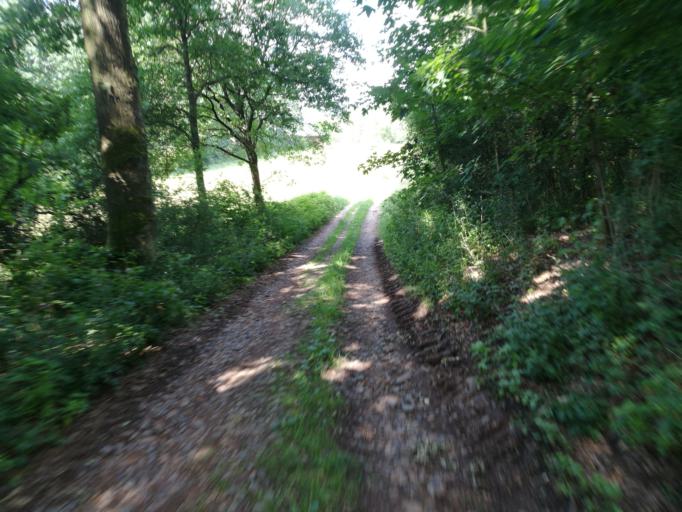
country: DE
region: Bavaria
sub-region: Regierungsbezirk Mittelfranken
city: Veitsbronn
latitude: 49.5005
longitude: 10.8892
